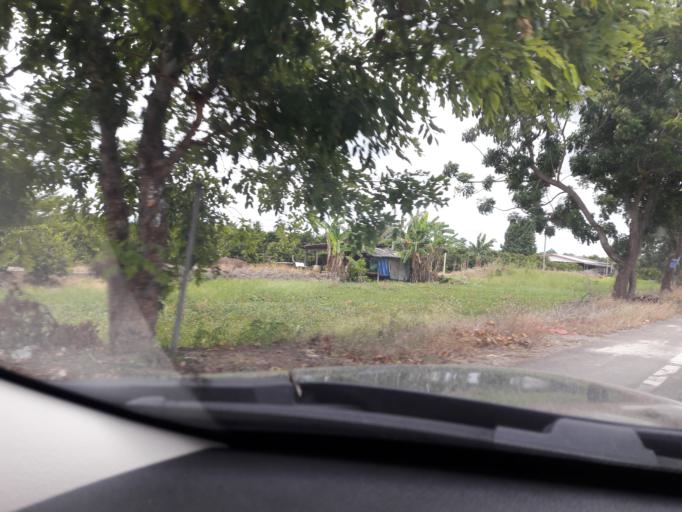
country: TH
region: Ratchaburi
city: Bang Phae
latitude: 13.6063
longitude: 99.9411
